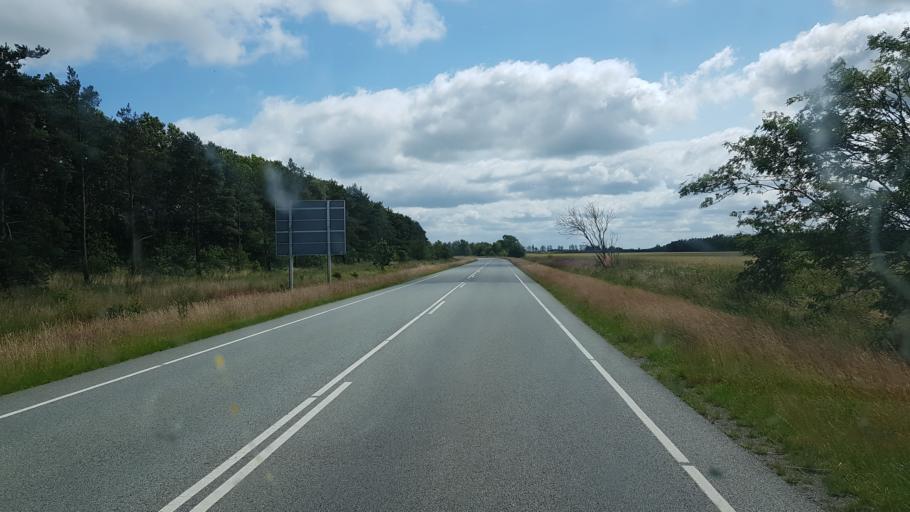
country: DK
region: South Denmark
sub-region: Billund Kommune
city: Grindsted
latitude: 55.7529
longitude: 8.9026
